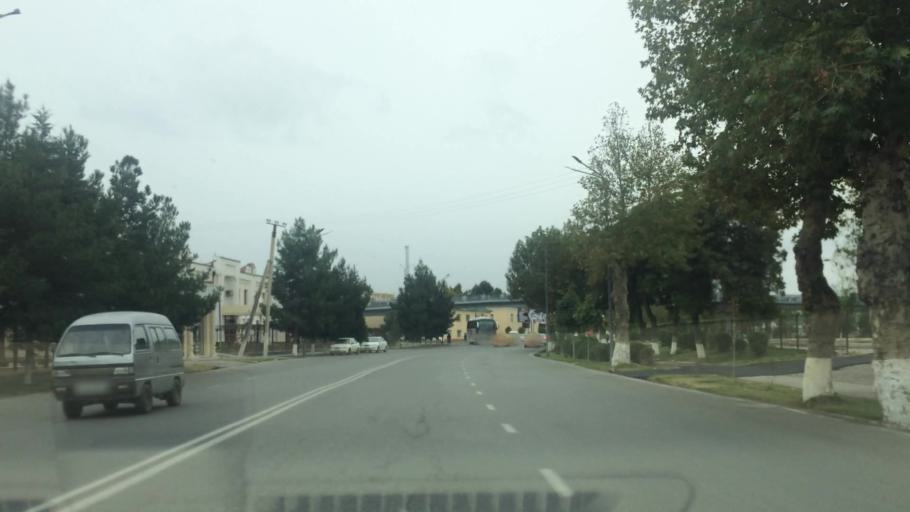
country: UZ
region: Samarqand
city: Samarqand
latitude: 39.6564
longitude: 66.9711
